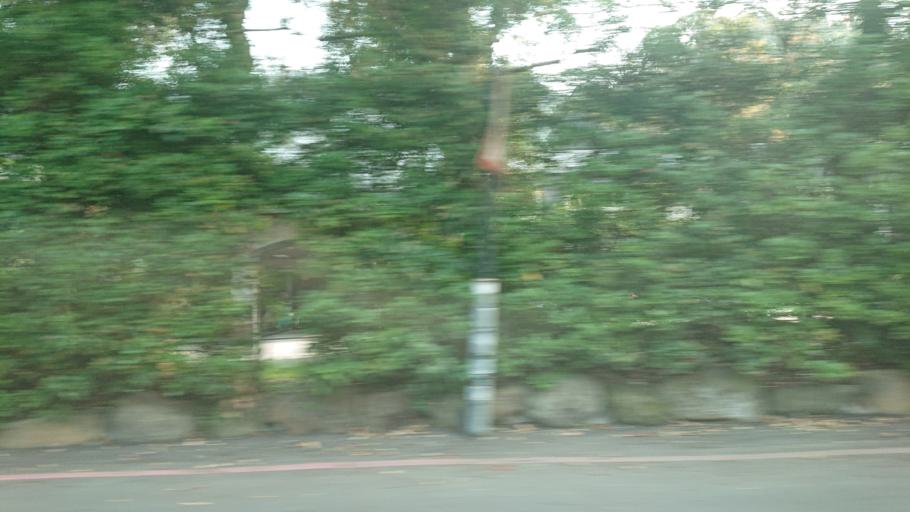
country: TW
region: Taiwan
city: Daxi
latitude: 24.8705
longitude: 121.4073
